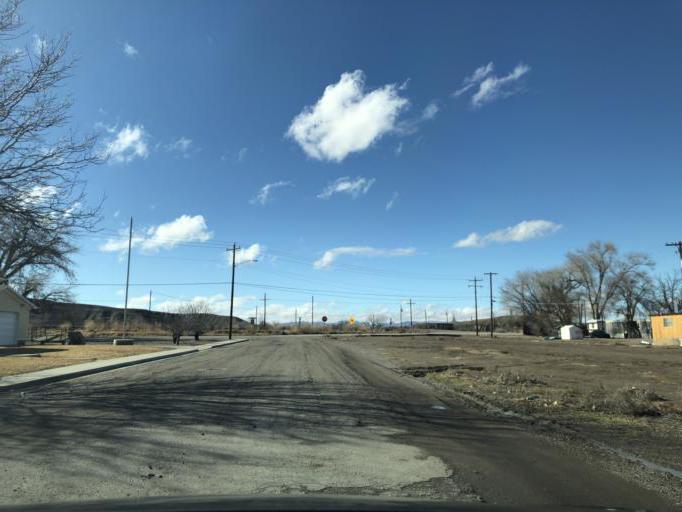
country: US
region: Utah
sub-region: Carbon County
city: East Carbon City
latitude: 38.9892
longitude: -110.1594
